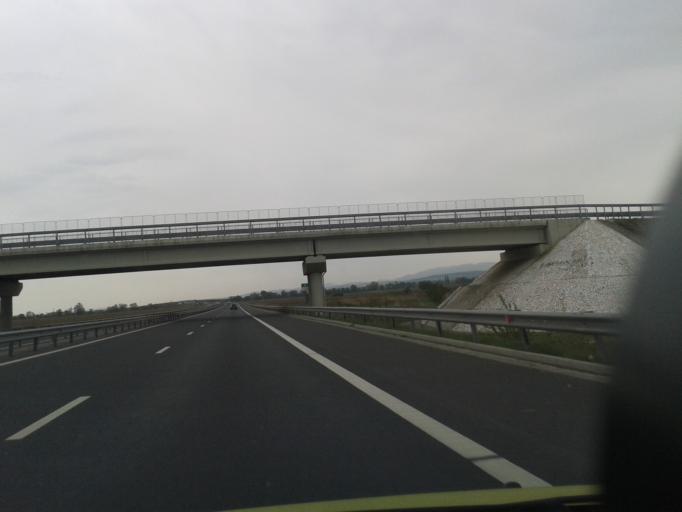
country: RO
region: Hunedoara
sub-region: Comuna Geoagiu
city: Geoagiu
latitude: 45.8820
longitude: 23.2192
